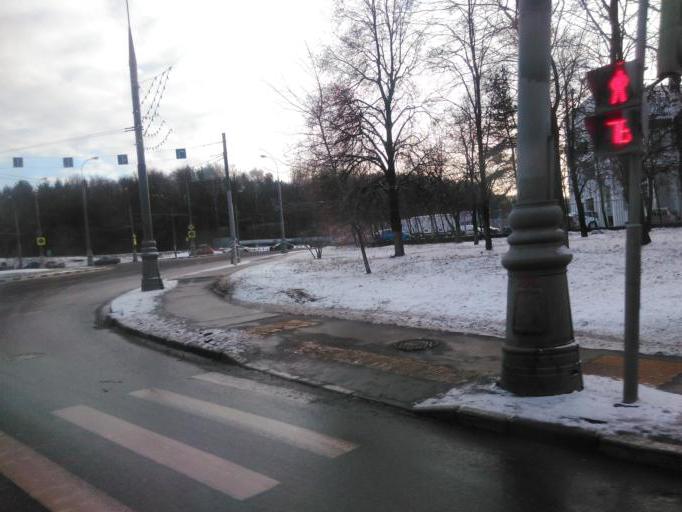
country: RU
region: Moscow
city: Zyuzino
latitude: 55.6496
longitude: 37.5627
